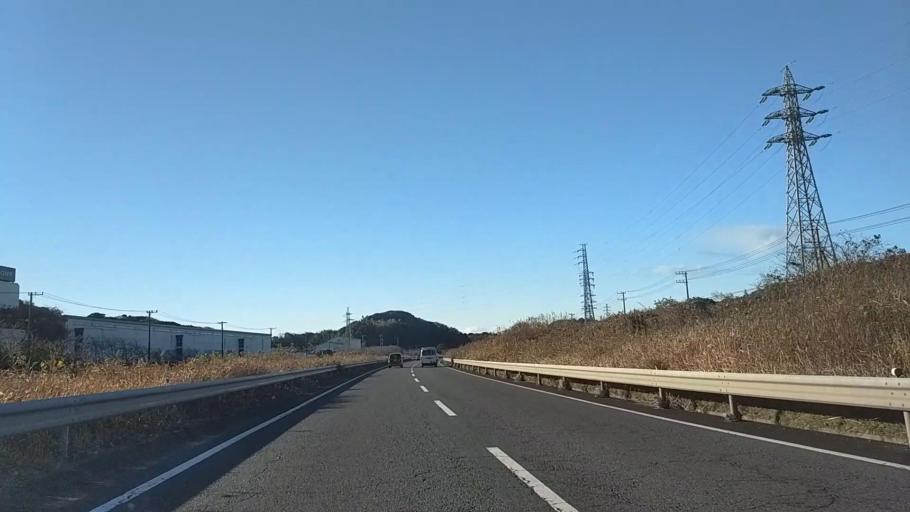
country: JP
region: Chiba
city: Kisarazu
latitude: 35.3603
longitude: 139.9107
